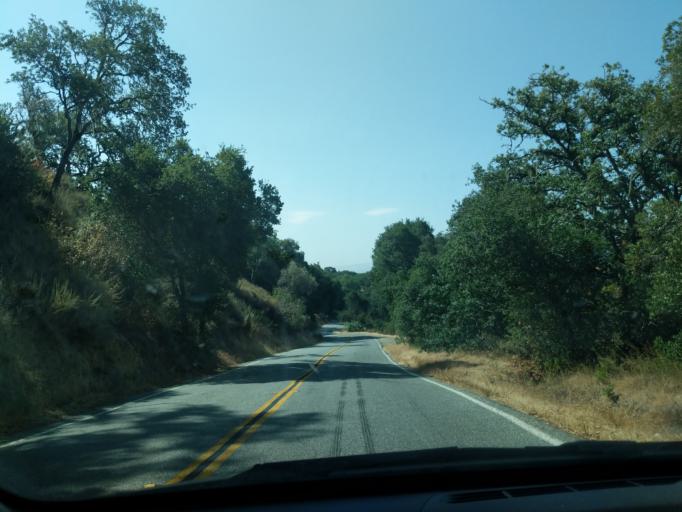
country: US
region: California
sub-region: Santa Clara County
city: Gilroy
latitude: 37.0603
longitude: -121.5204
